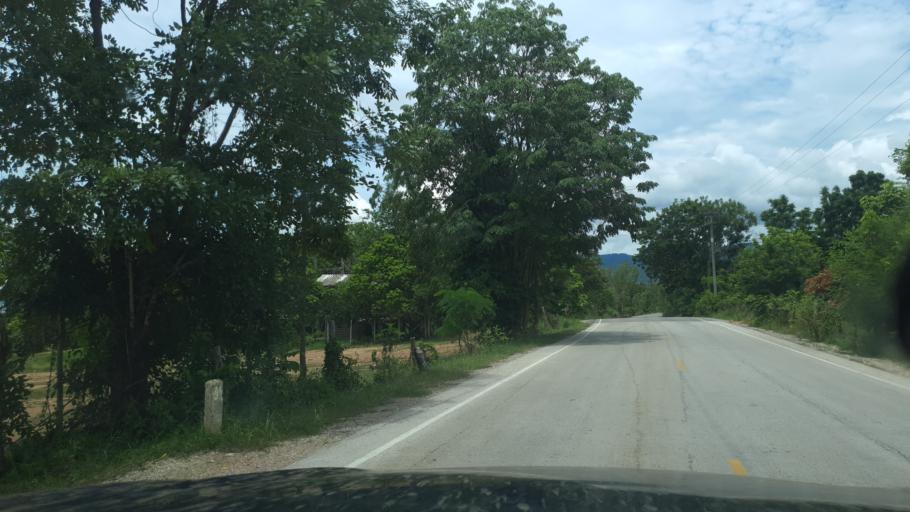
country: TH
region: Lampang
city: Sop Prap
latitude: 17.9140
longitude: 99.3936
